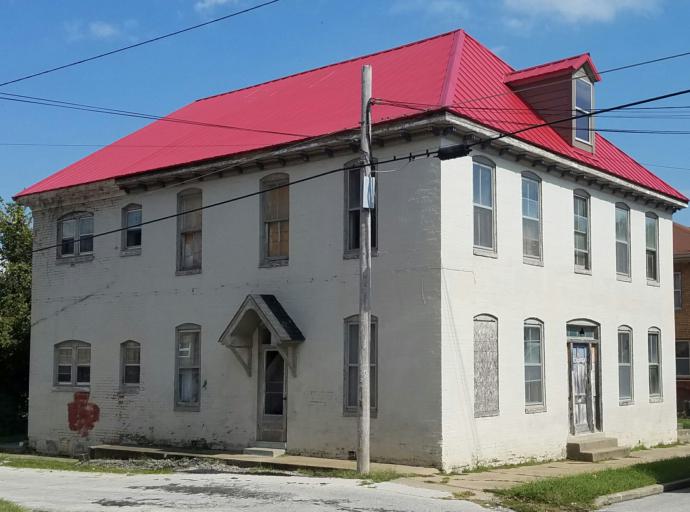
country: US
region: Missouri
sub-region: Cooper County
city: Boonville
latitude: 38.9738
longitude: -92.7427
